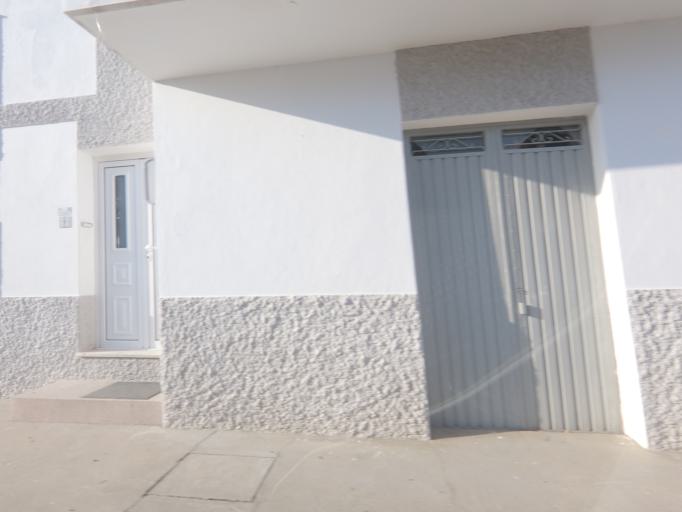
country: PT
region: Vila Real
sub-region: Sabrosa
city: Vilela
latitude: 41.2699
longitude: -7.6641
